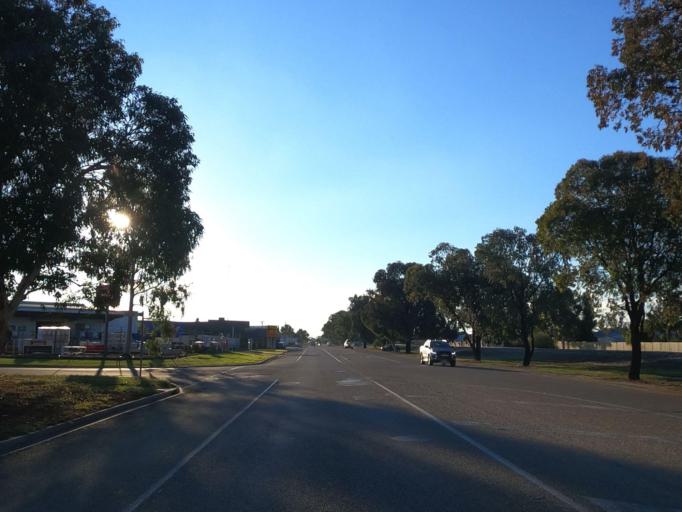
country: AU
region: Victoria
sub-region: Swan Hill
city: Swan Hill
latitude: -35.3322
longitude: 143.5579
